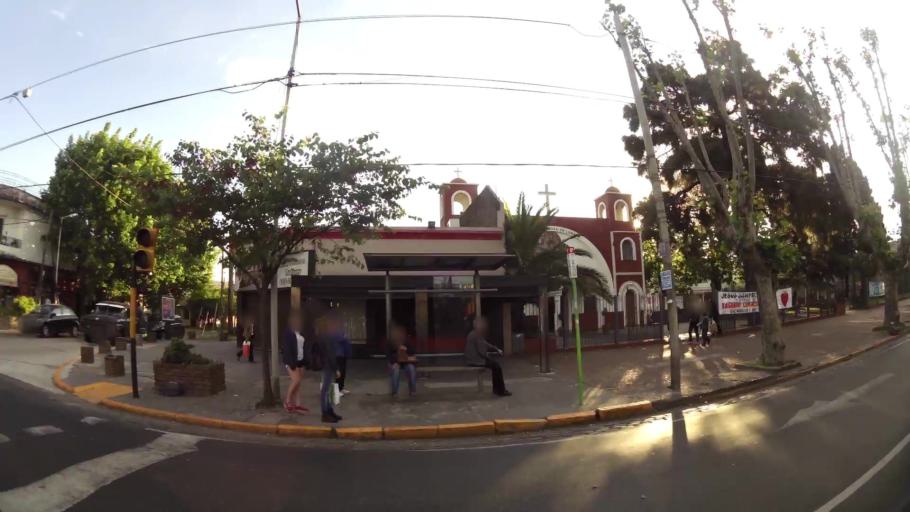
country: AR
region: Buenos Aires
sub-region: Partido de Avellaneda
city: Avellaneda
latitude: -34.6873
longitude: -58.3397
